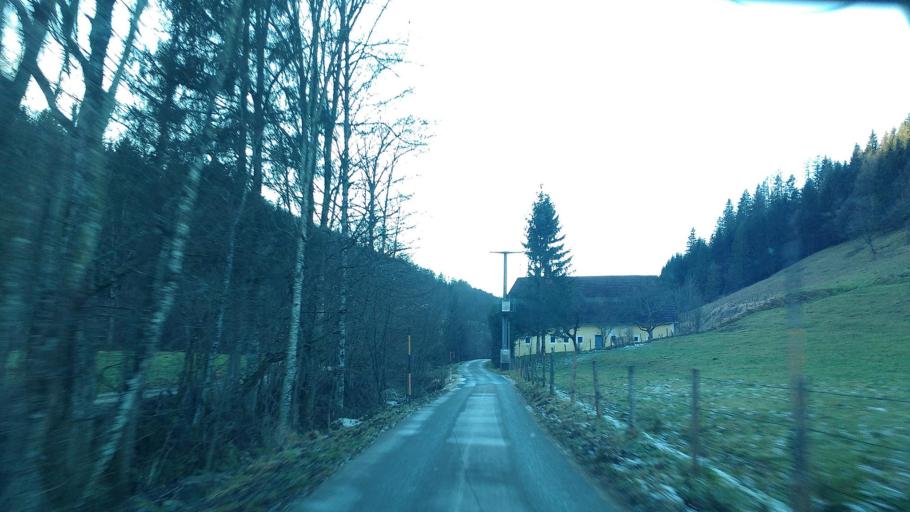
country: AT
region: Upper Austria
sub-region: Politischer Bezirk Kirchdorf an der Krems
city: Micheldorf in Oberoesterreich
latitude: 47.9019
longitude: 14.1973
